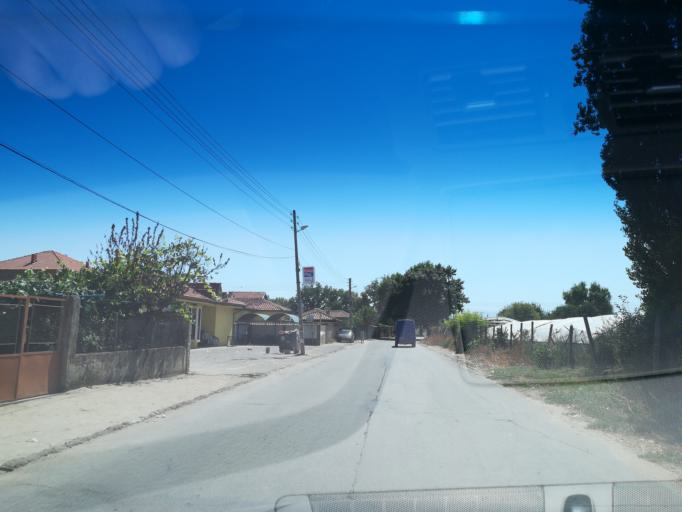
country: BG
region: Pazardzhik
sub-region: Obshtina Pazardzhik
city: Pazardzhik
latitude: 42.2743
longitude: 24.3967
